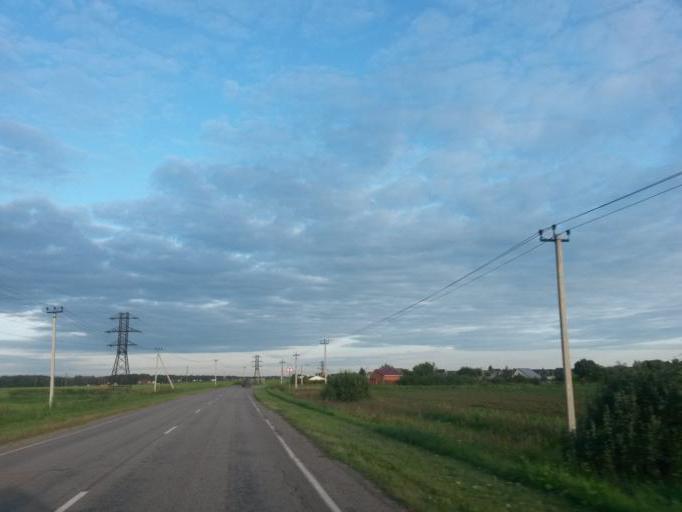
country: RU
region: Moskovskaya
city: Belyye Stolby
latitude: 55.2493
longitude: 37.7918
